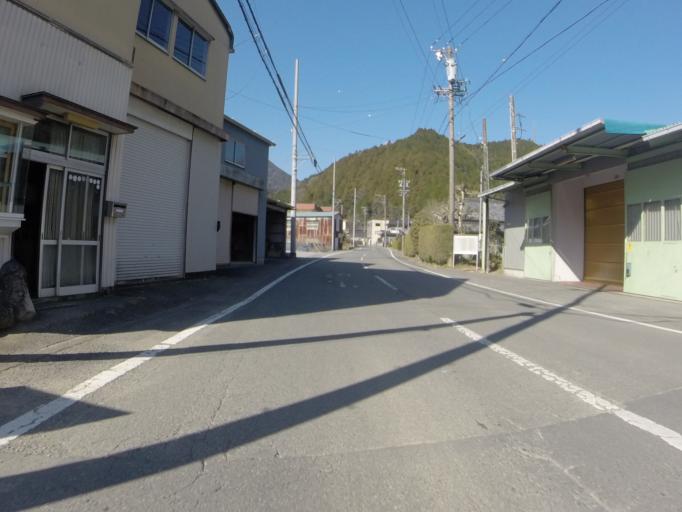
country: JP
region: Shizuoka
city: Fujinomiya
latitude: 35.1232
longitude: 138.4795
